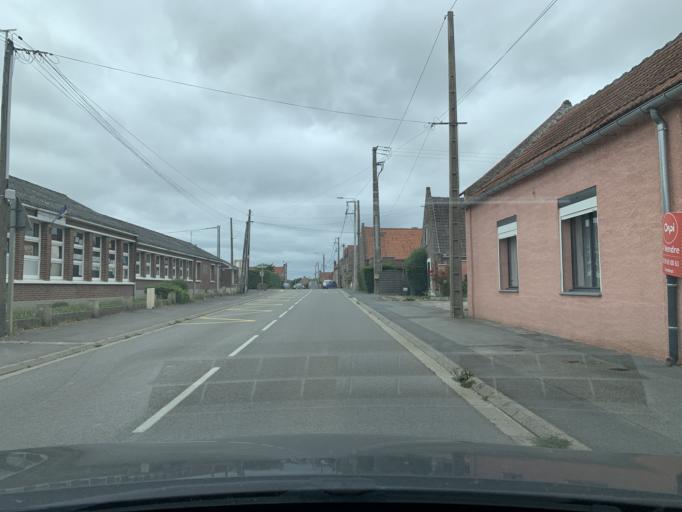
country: FR
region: Nord-Pas-de-Calais
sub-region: Departement du Nord
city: Fechain
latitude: 50.2544
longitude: 3.1930
